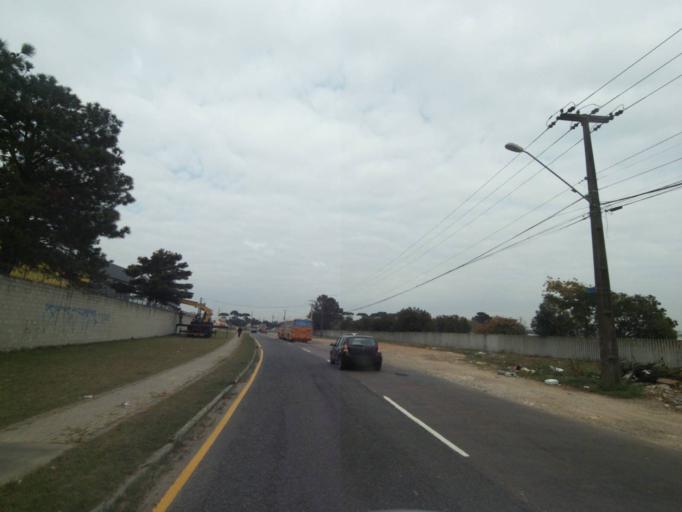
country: BR
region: Parana
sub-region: Curitiba
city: Curitiba
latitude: -25.5180
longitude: -49.3271
